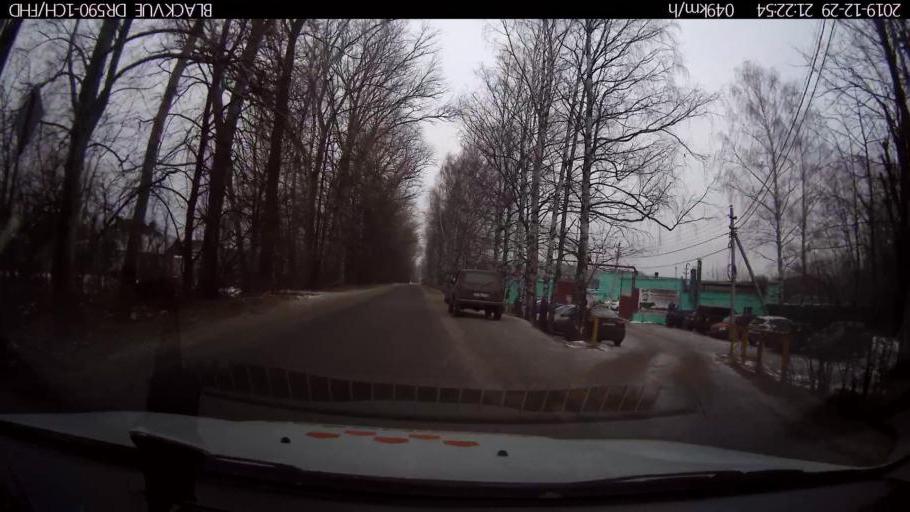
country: RU
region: Nizjnij Novgorod
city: Afonino
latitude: 56.2185
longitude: 44.0365
